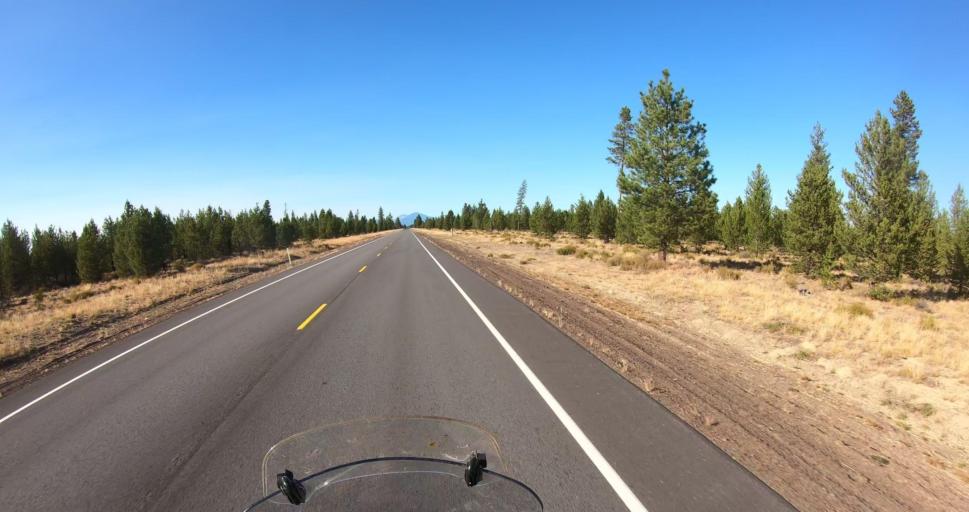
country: US
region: Oregon
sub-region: Deschutes County
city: La Pine
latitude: 43.6111
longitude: -121.5033
